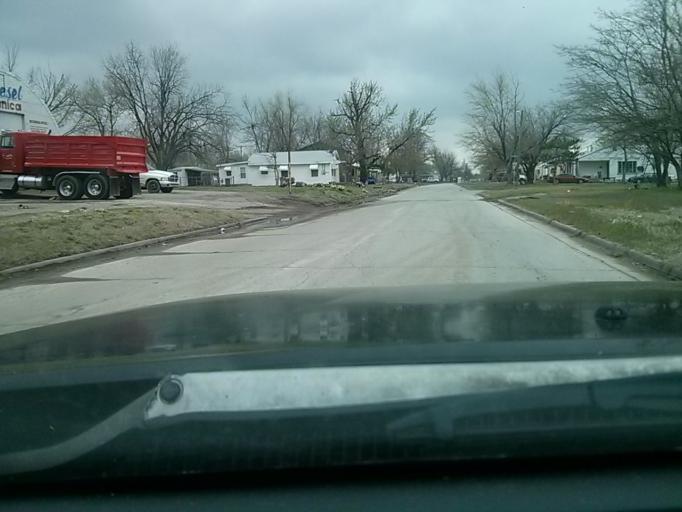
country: US
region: Oklahoma
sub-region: Tulsa County
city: Tulsa
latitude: 36.1632
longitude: -95.9135
